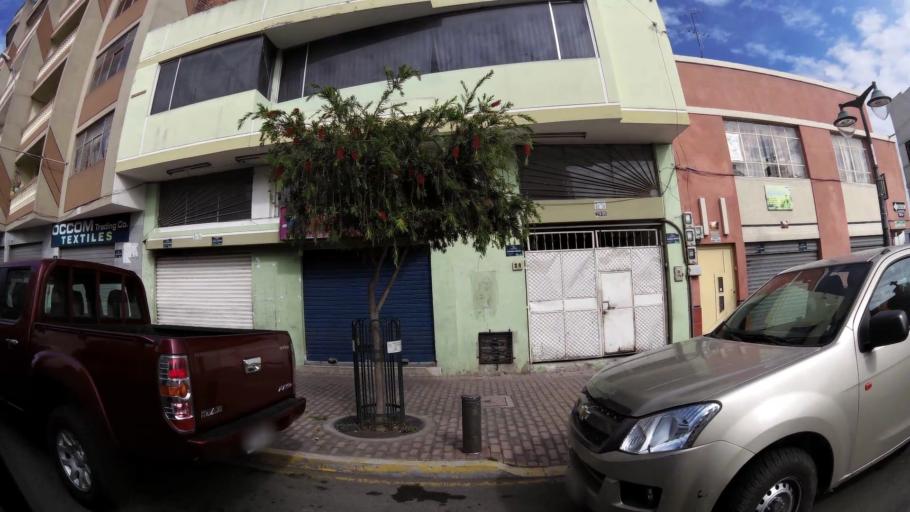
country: EC
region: Tungurahua
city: Ambato
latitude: -1.2536
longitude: -78.6457
